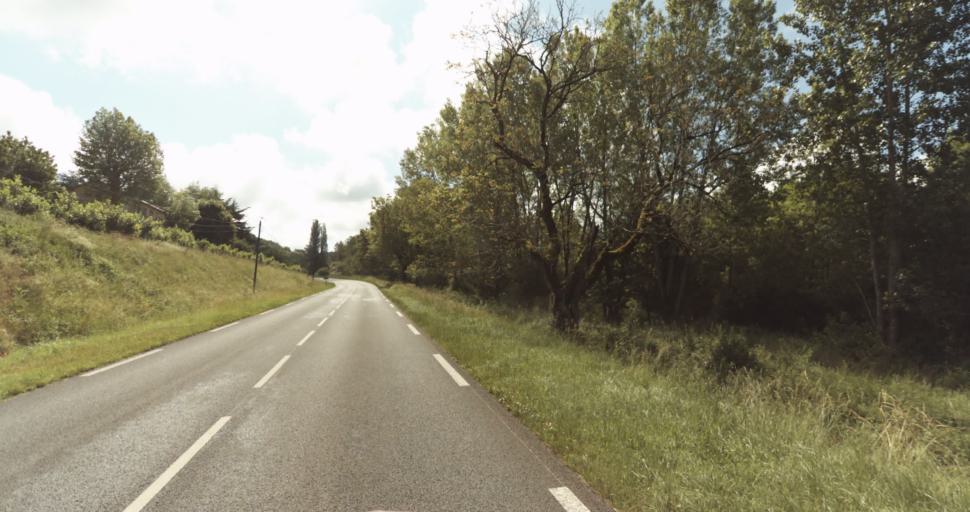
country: FR
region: Aquitaine
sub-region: Departement de la Dordogne
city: Le Bugue
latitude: 44.8414
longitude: 0.8530
